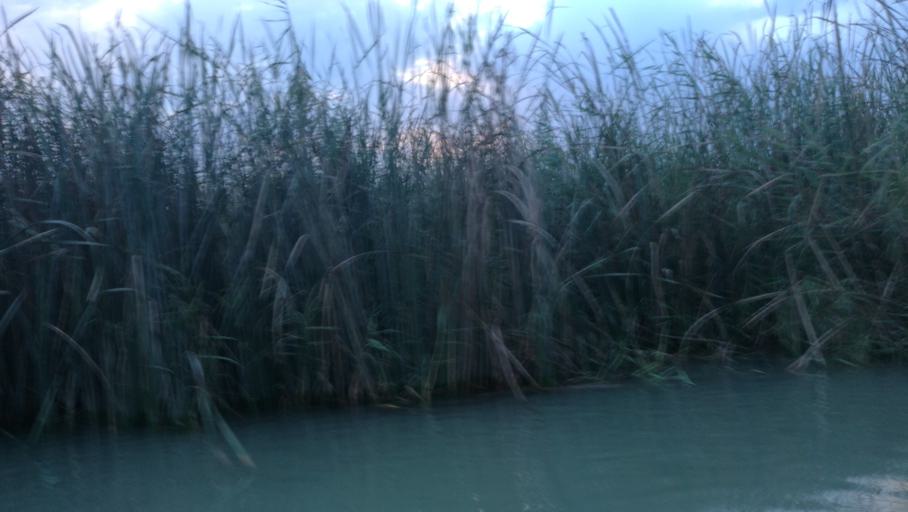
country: IQ
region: Dhi Qar
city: Al Jabayish
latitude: 30.9808
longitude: 47.0372
